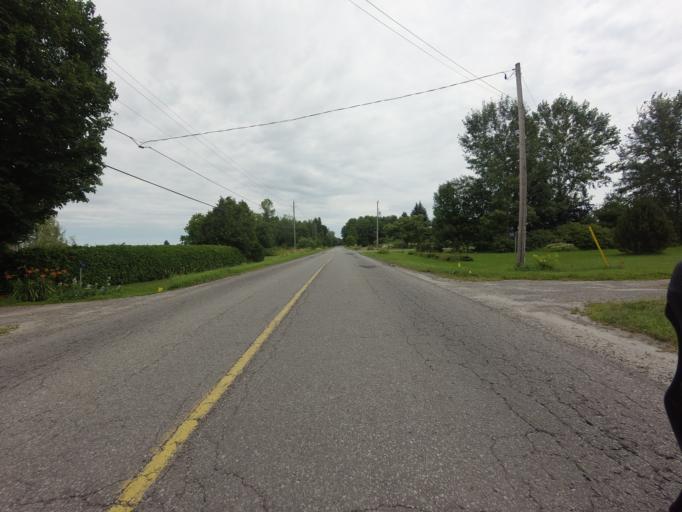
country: CA
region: Ontario
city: Bells Corners
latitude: 45.0245
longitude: -75.7022
